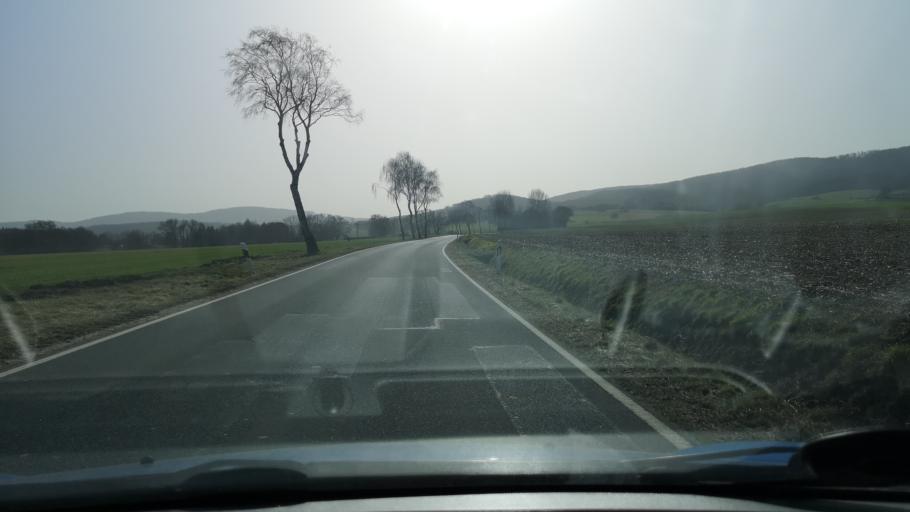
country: DE
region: Lower Saxony
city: Weenzen
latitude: 52.0103
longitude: 9.6334
